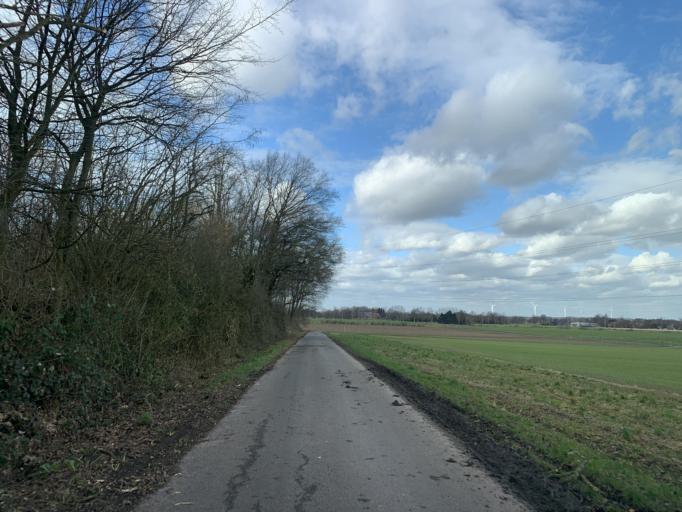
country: DE
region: North Rhine-Westphalia
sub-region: Regierungsbezirk Munster
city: Horstmar
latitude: 52.0969
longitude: 7.3101
